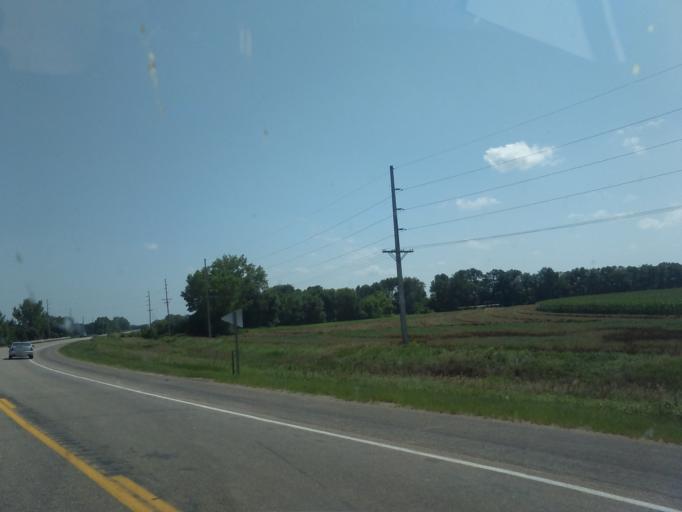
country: US
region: Nebraska
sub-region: Phelps County
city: Holdrege
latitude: 40.7108
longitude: -99.3795
